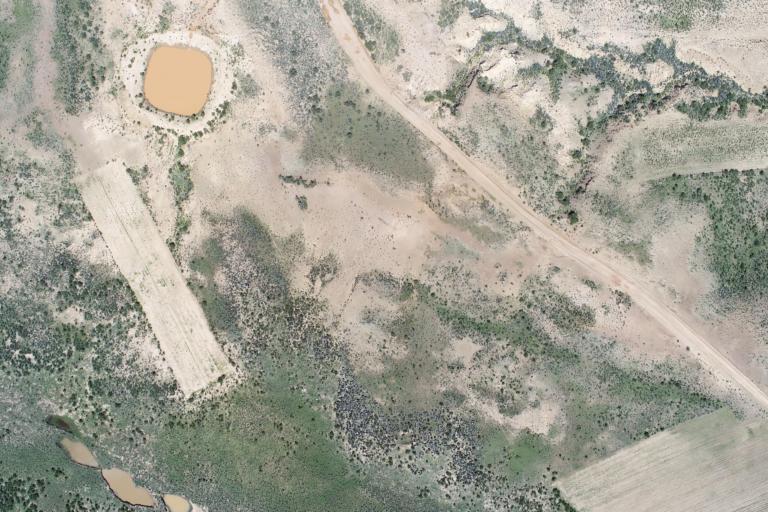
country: BO
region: La Paz
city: Curahuara de Carangas
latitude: -17.2953
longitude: -68.5151
